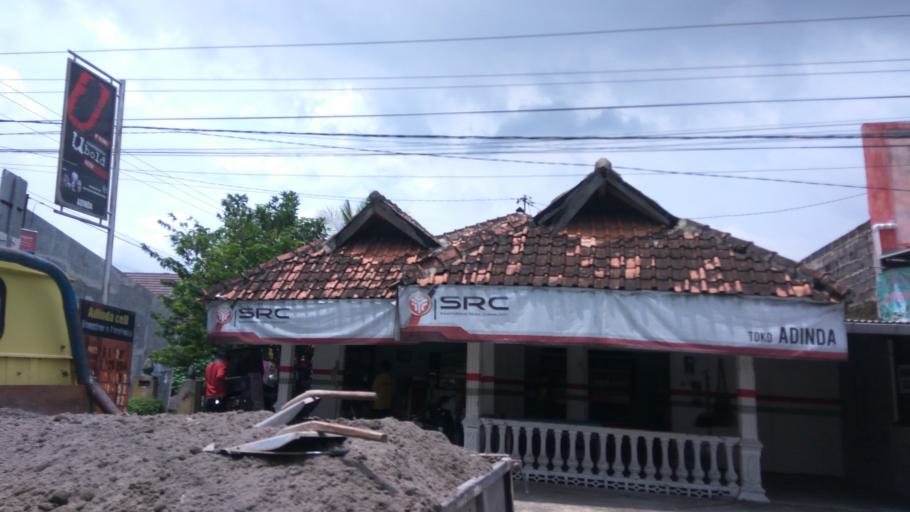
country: ID
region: Daerah Istimewa Yogyakarta
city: Melati
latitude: -7.7283
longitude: 110.3800
